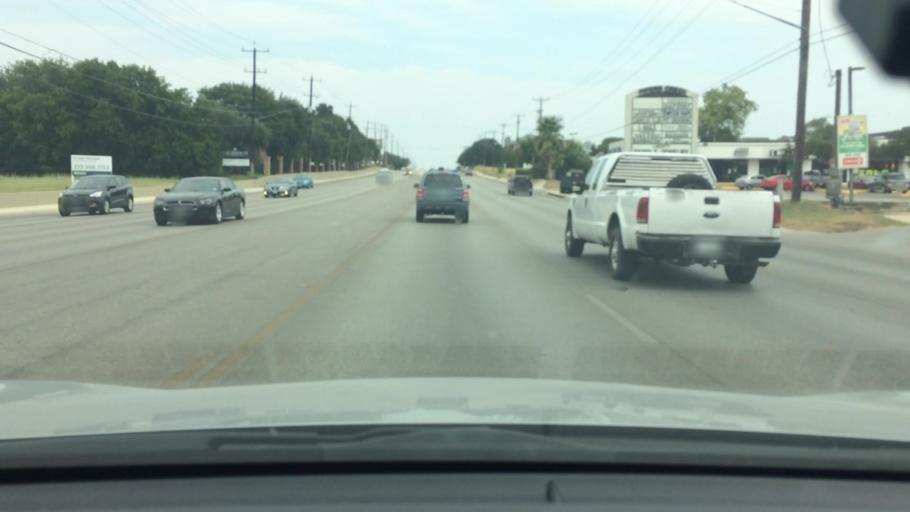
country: US
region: Texas
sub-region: Bexar County
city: Leon Valley
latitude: 29.4636
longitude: -98.6436
